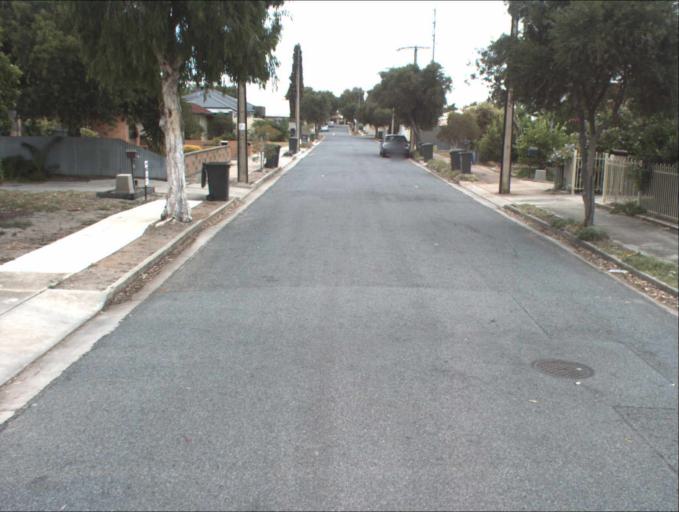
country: AU
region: South Australia
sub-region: Port Adelaide Enfield
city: Birkenhead
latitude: -34.7975
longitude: 138.4978
